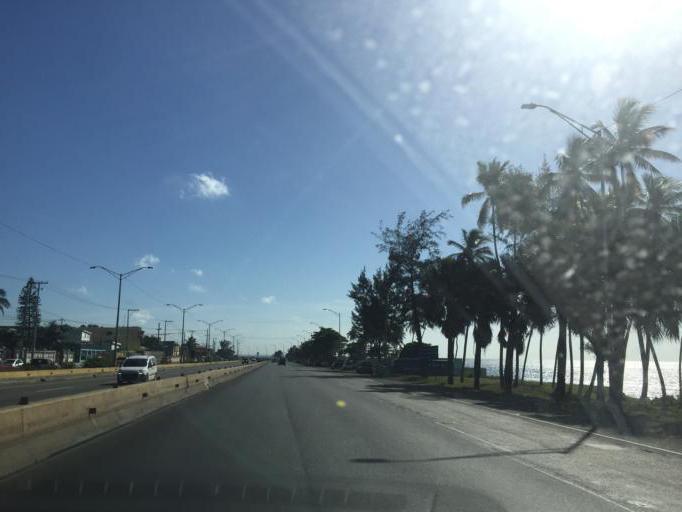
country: DO
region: Santo Domingo
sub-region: Santo Domingo
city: Santo Domingo Este
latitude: 18.4663
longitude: -69.8234
